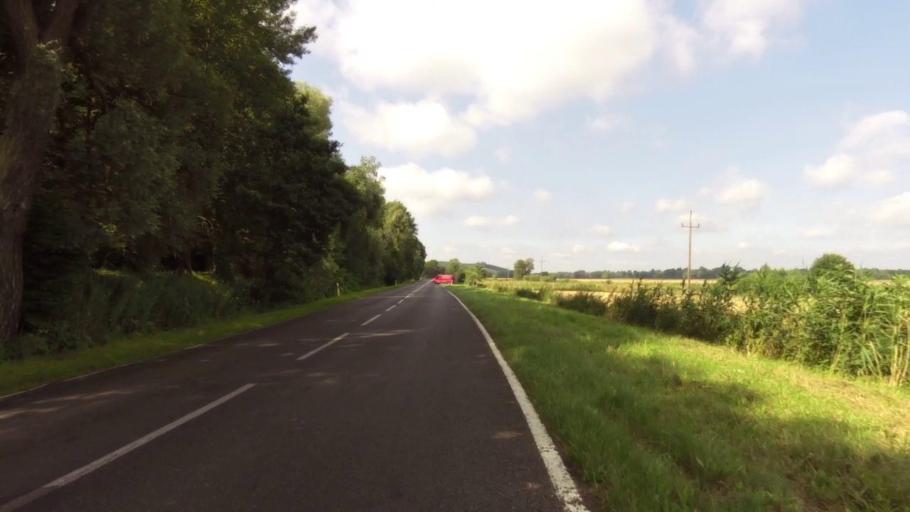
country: PL
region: West Pomeranian Voivodeship
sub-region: Powiat gryfinski
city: Cedynia
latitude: 52.8678
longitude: 14.1867
